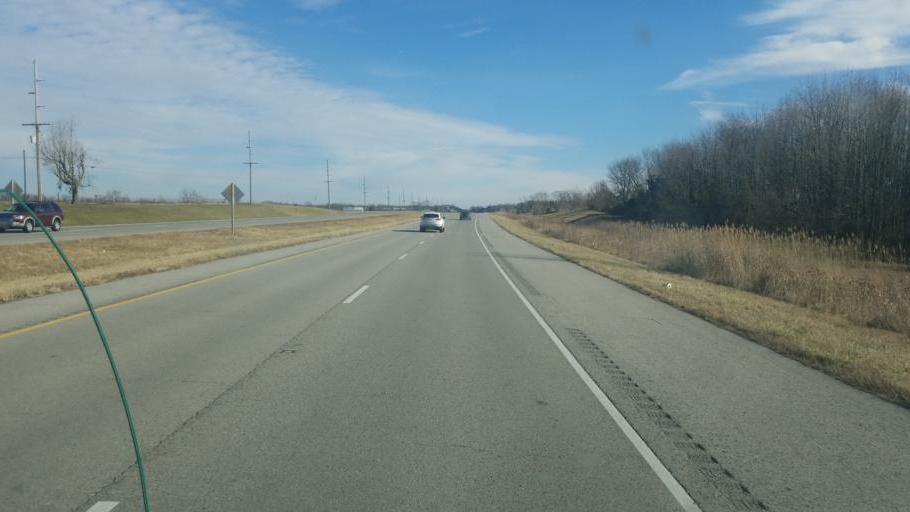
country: US
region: Illinois
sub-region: Williamson County
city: Marion
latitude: 37.7295
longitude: -88.8478
